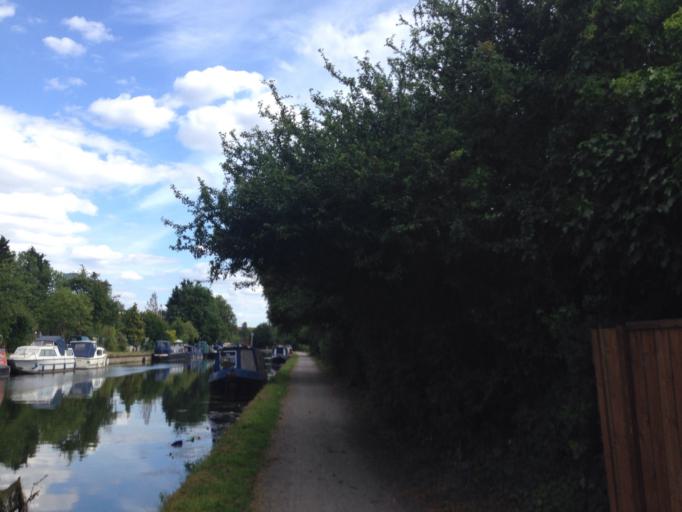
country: GB
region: England
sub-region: Greater London
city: Wembley
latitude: 51.5423
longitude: -0.3079
